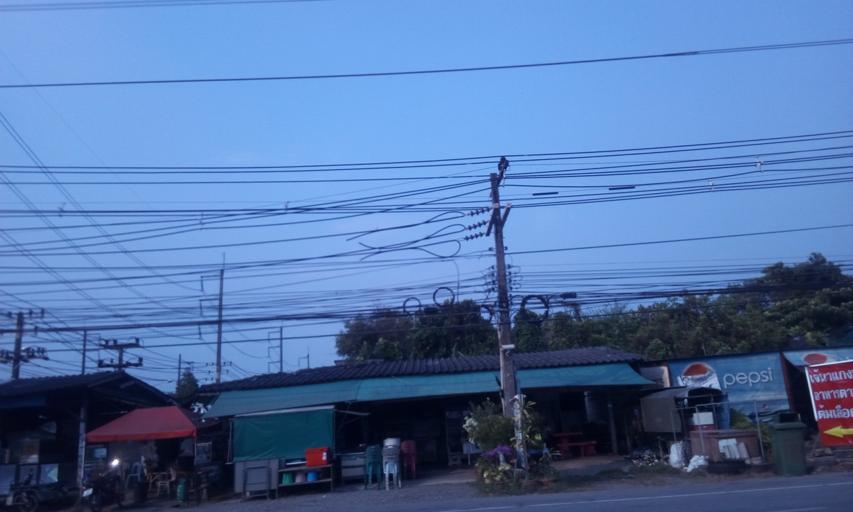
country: TH
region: Chanthaburi
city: Khlung
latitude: 12.4601
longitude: 102.2304
